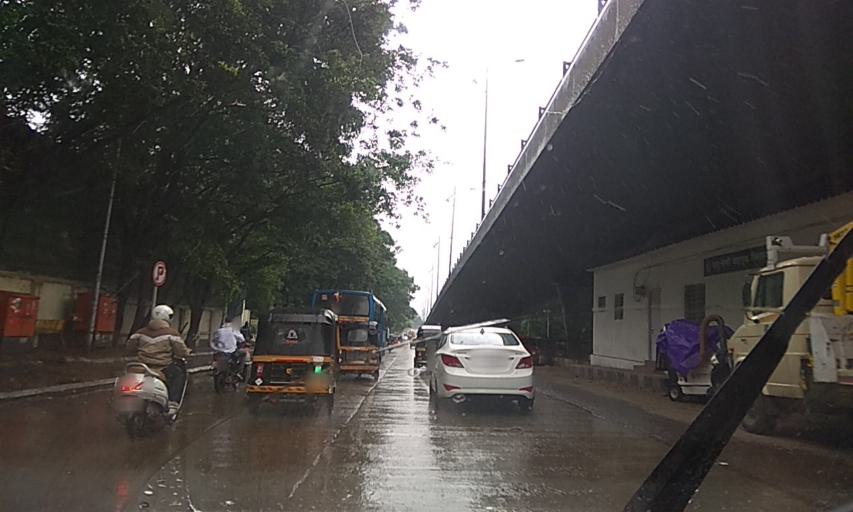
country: IN
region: Maharashtra
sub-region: Pune Division
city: Shivaji Nagar
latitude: 18.5407
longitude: 73.8310
